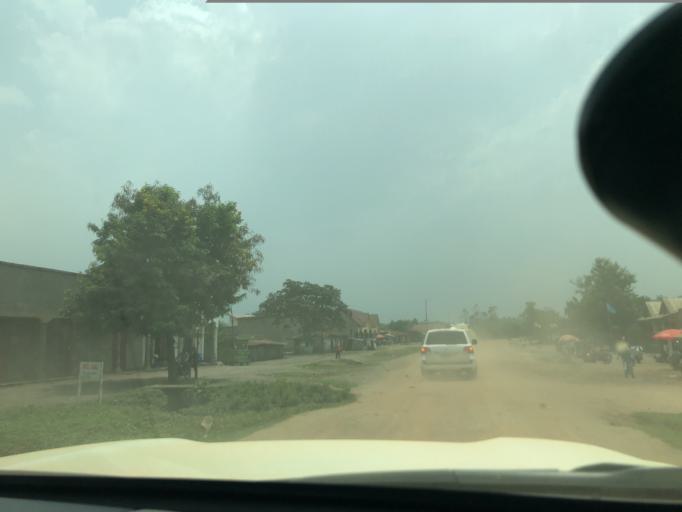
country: UG
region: Western Region
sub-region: Kasese District
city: Margherita
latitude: 0.3279
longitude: 29.6762
